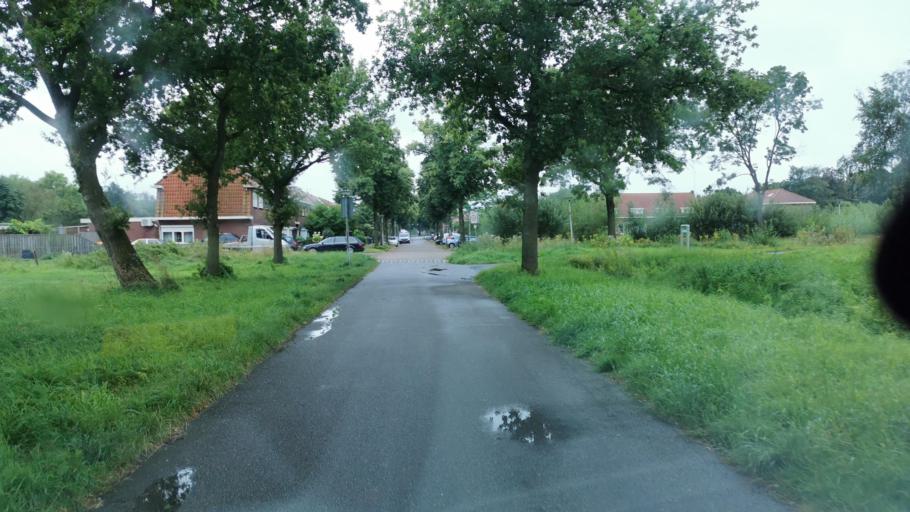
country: NL
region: Overijssel
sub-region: Gemeente Enschede
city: Enschede
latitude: 52.2201
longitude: 6.9461
